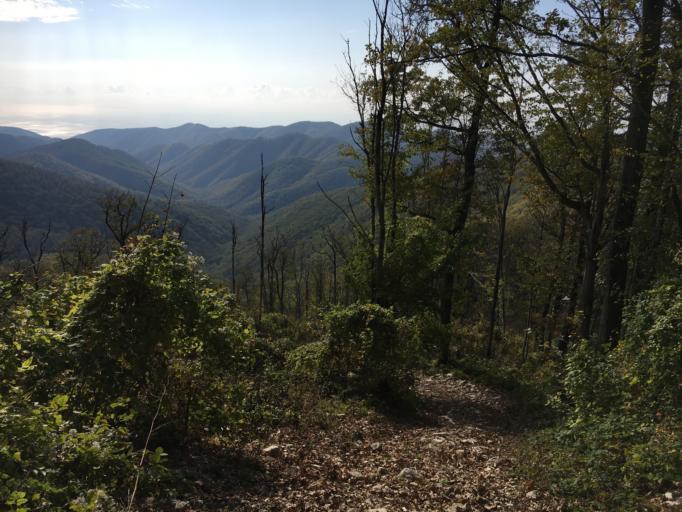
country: RU
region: Krasnodarskiy
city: Nebug
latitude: 44.2404
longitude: 38.9853
